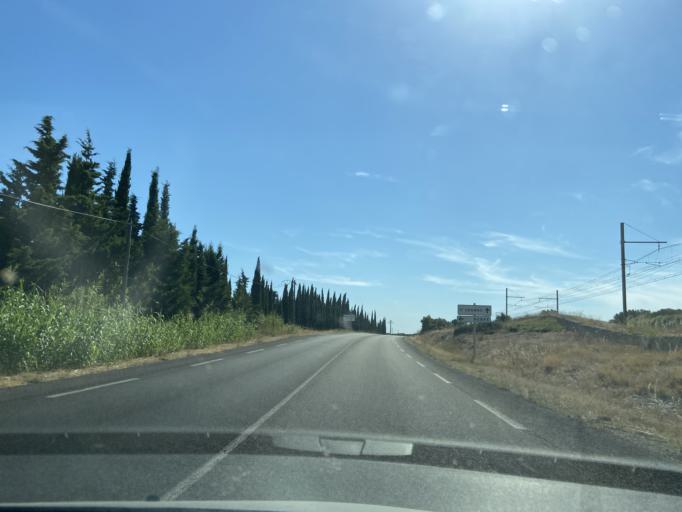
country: FR
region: Provence-Alpes-Cote d'Azur
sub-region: Departement des Bouches-du-Rhone
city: Cornillon-Confoux
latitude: 43.5318
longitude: 5.1054
